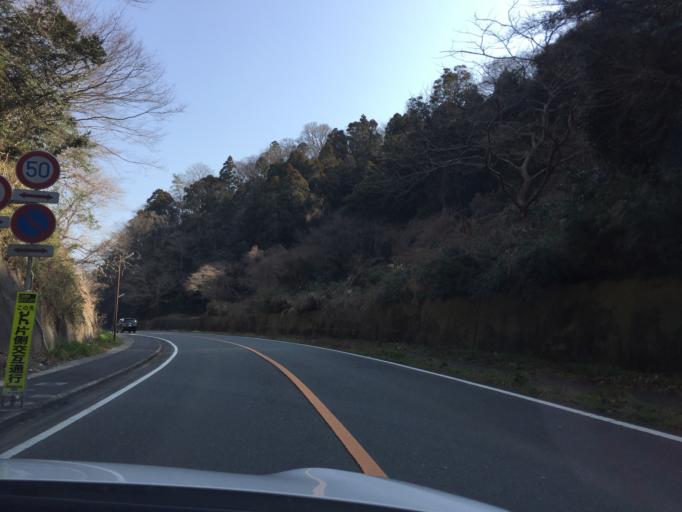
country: JP
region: Fukushima
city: Iwaki
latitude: 36.9644
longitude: 140.9512
